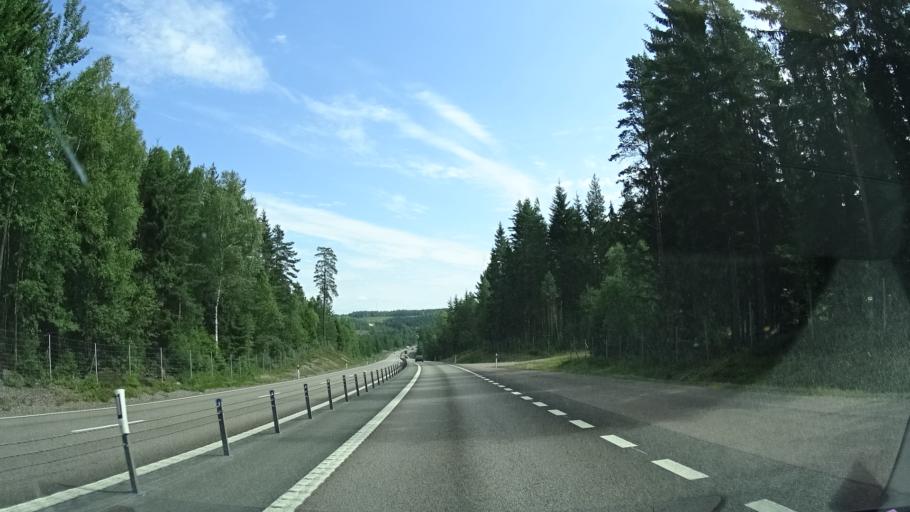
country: SE
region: Vaermland
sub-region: Kristinehamns Kommun
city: Bjorneborg
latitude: 59.3099
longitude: 14.3005
